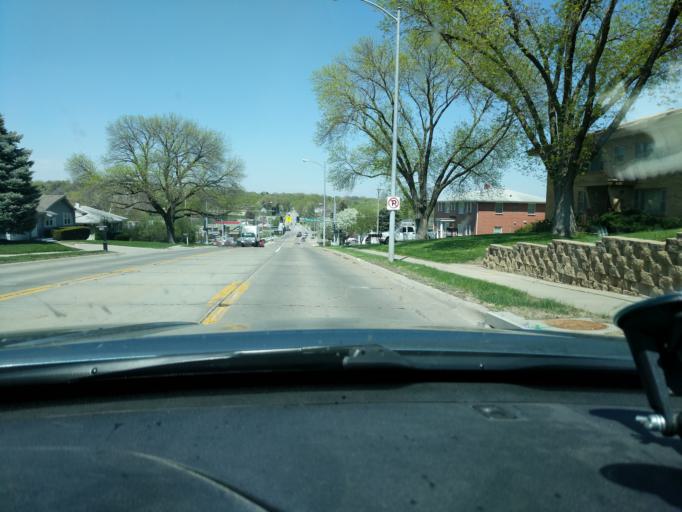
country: US
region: Nebraska
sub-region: Douglas County
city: Ralston
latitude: 41.2311
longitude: -96.0815
